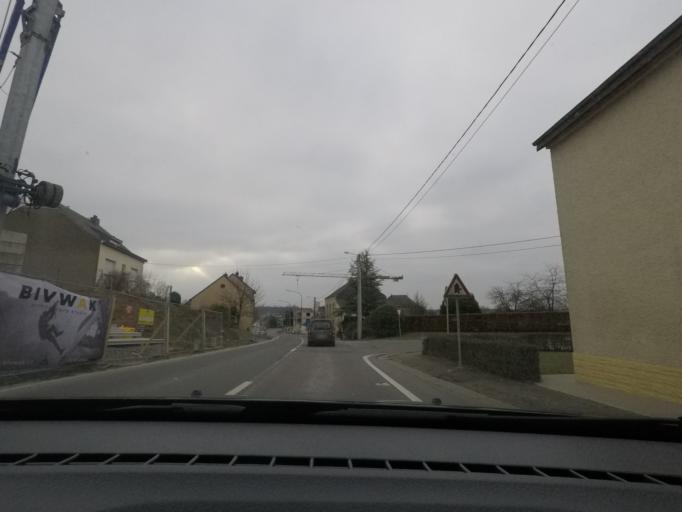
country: BE
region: Wallonia
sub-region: Province du Luxembourg
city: Etalle
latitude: 49.6763
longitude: 5.6045
